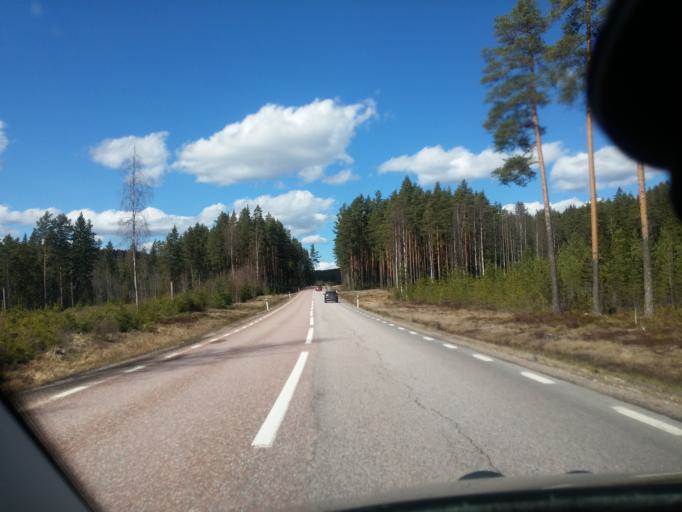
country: SE
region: Dalarna
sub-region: Faluns Kommun
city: Svardsjo
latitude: 60.7552
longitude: 15.7591
